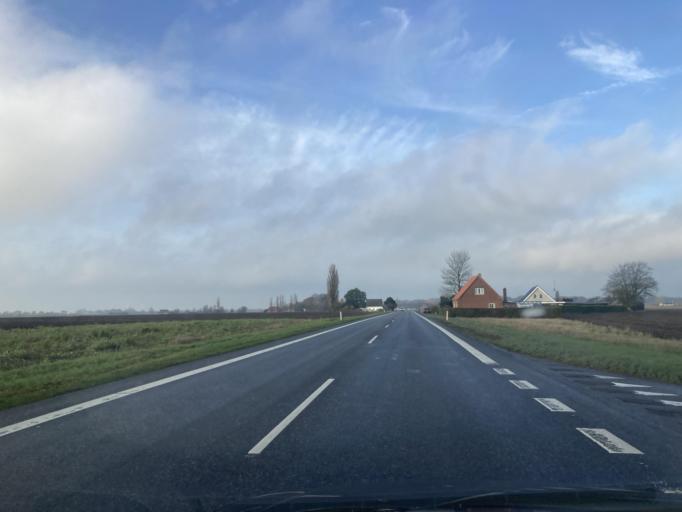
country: DK
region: Zealand
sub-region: Lolland Kommune
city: Rodby
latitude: 54.7516
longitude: 11.3754
